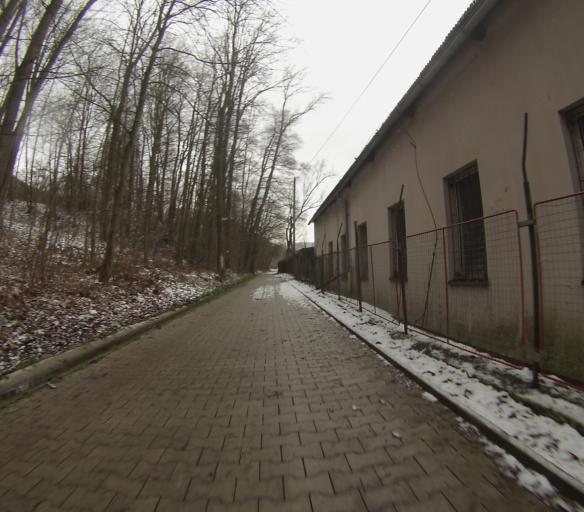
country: CZ
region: Ustecky
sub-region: Okres Decin
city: Decin
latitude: 50.7586
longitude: 14.2573
